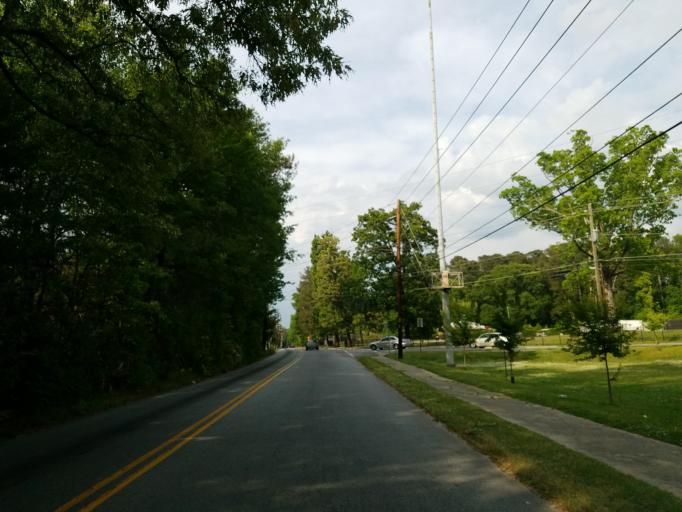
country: US
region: Georgia
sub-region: Cobb County
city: Vinings
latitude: 33.7920
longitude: -84.4940
